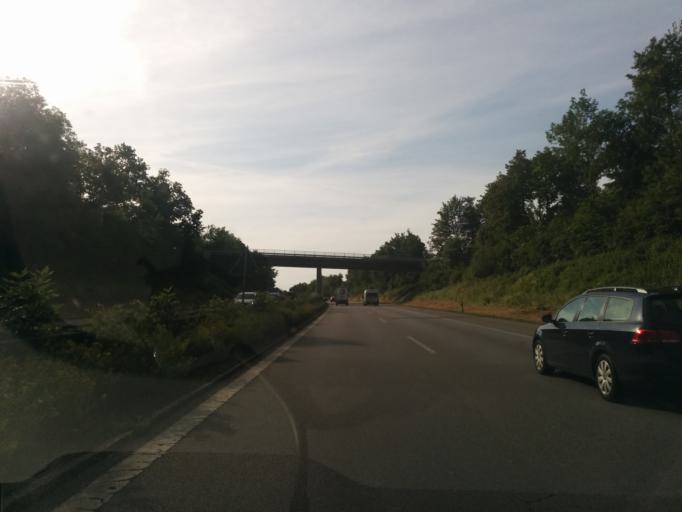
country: DE
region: Bavaria
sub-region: Upper Bavaria
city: Landsberg am Lech
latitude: 48.0612
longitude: 10.8812
